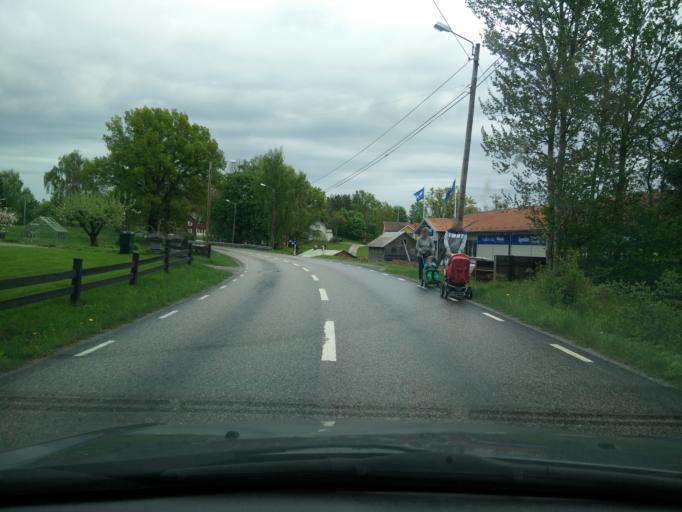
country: SE
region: Stockholm
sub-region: Norrtalje Kommun
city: Bjorko
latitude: 59.8085
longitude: 18.8921
